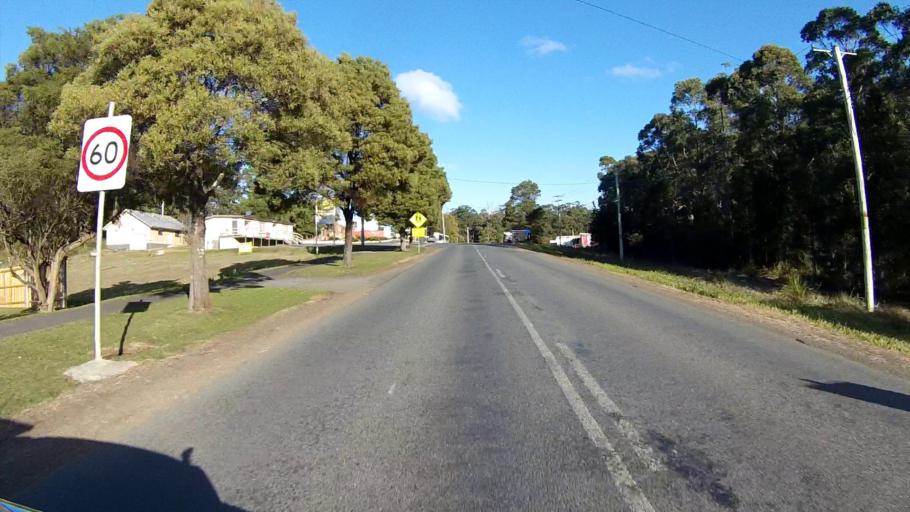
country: AU
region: Tasmania
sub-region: Clarence
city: Sandford
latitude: -43.1387
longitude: 147.8507
